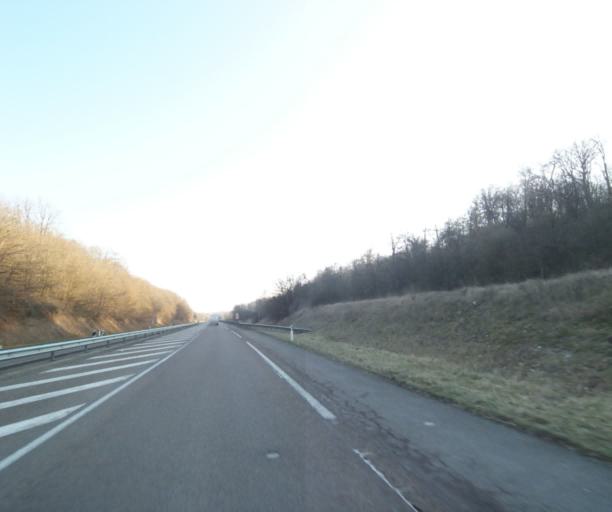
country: FR
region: Champagne-Ardenne
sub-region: Departement de la Haute-Marne
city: Chevillon
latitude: 48.5044
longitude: 5.1017
